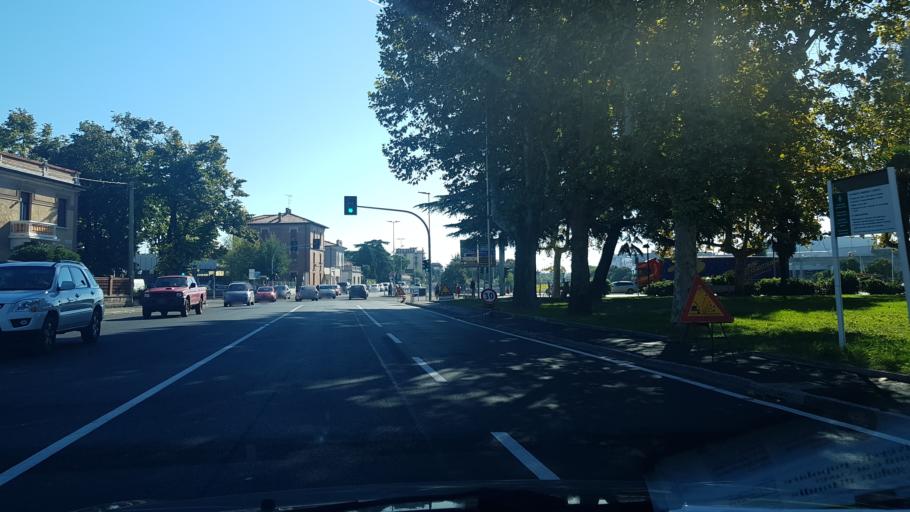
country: IT
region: Friuli Venezia Giulia
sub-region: Provincia di Gorizia
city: Monfalcone
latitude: 45.8052
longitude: 13.5321
